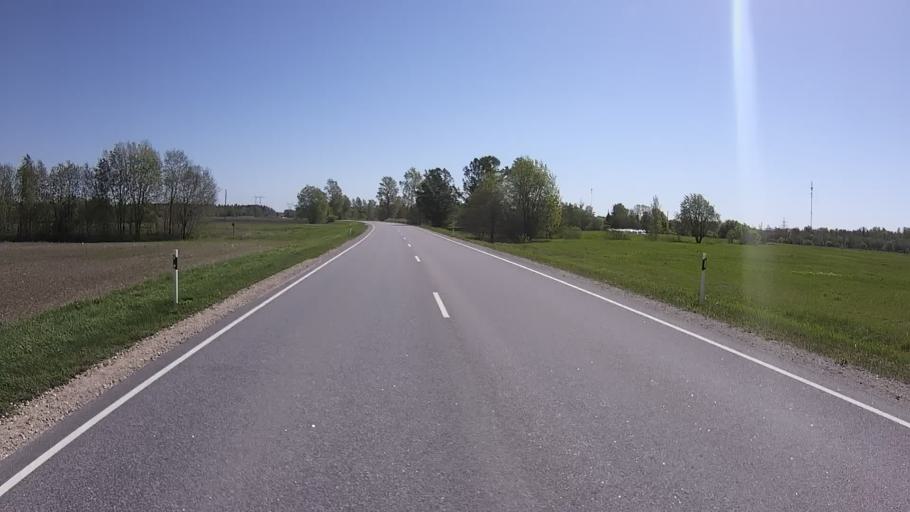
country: EE
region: Paernumaa
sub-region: Audru vald
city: Audru
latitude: 58.4235
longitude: 24.3005
